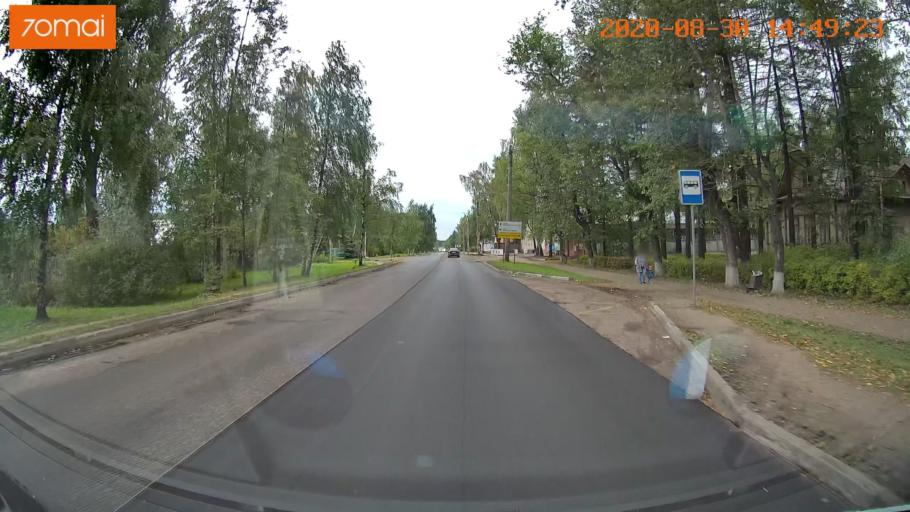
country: RU
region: Ivanovo
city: Kineshma
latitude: 57.4336
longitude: 42.1092
